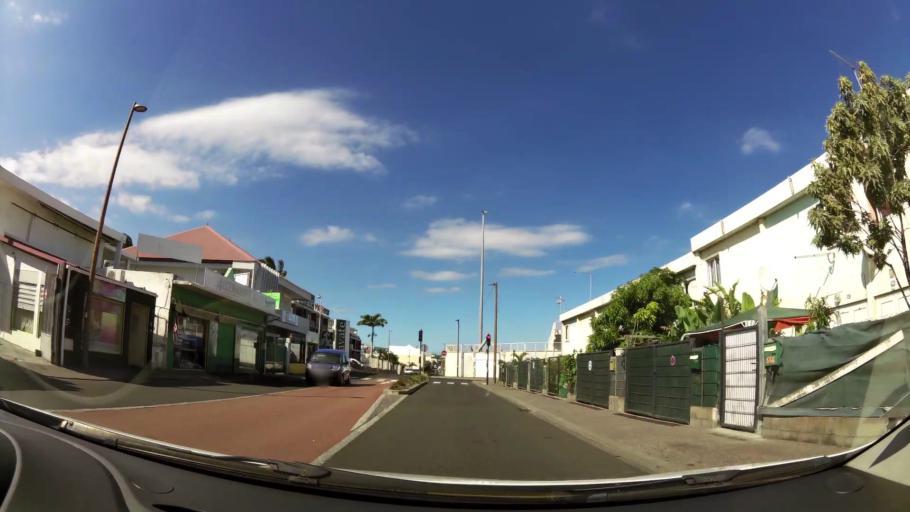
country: RE
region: Reunion
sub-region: Reunion
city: Saint-Pierre
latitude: -21.3378
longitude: 55.4670
